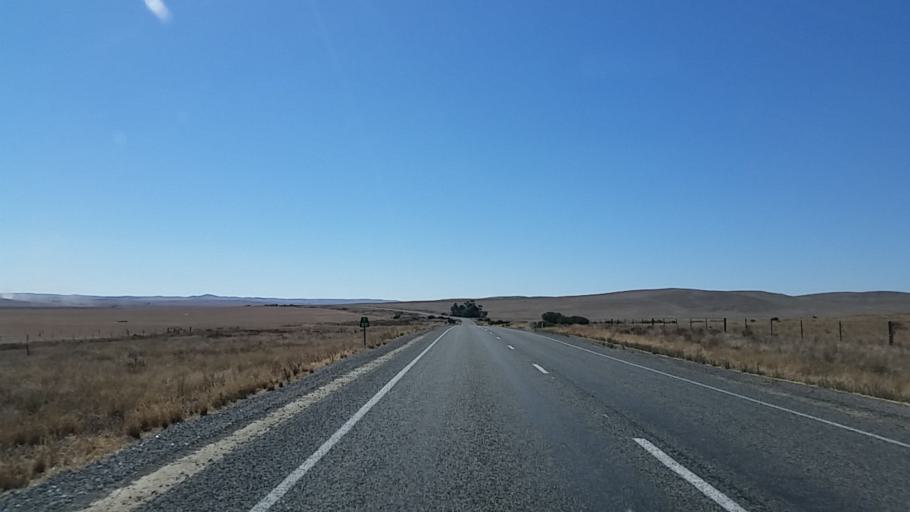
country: AU
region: South Australia
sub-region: Northern Areas
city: Jamestown
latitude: -33.3161
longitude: 138.8828
